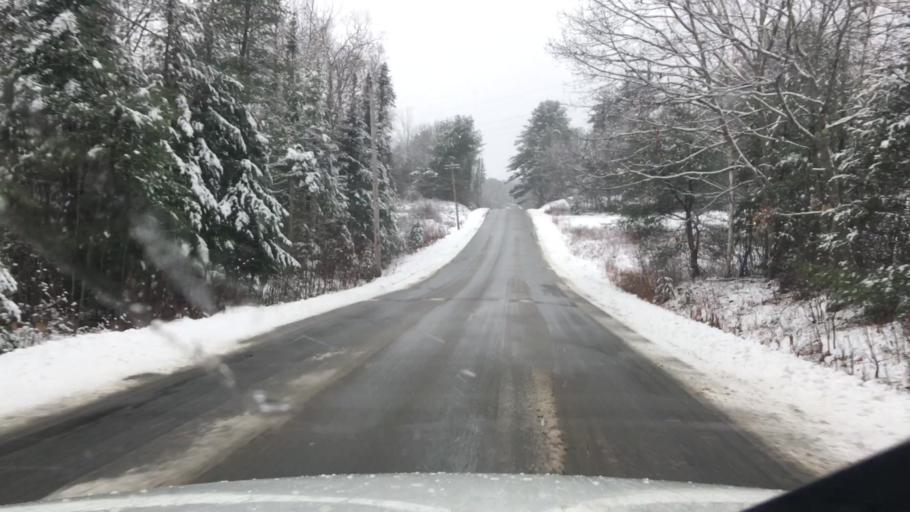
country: US
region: Maine
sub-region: Knox County
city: Union
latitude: 44.1720
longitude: -69.3292
